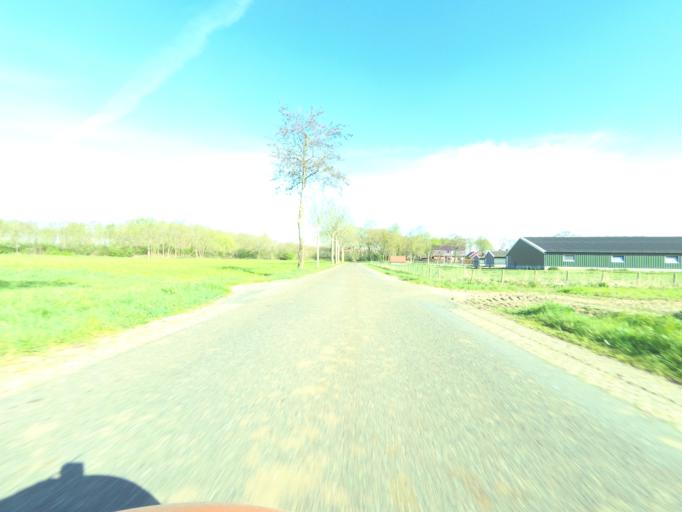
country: NL
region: Gelderland
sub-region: Gemeente Ermelo
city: Horst
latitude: 52.3099
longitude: 5.5658
